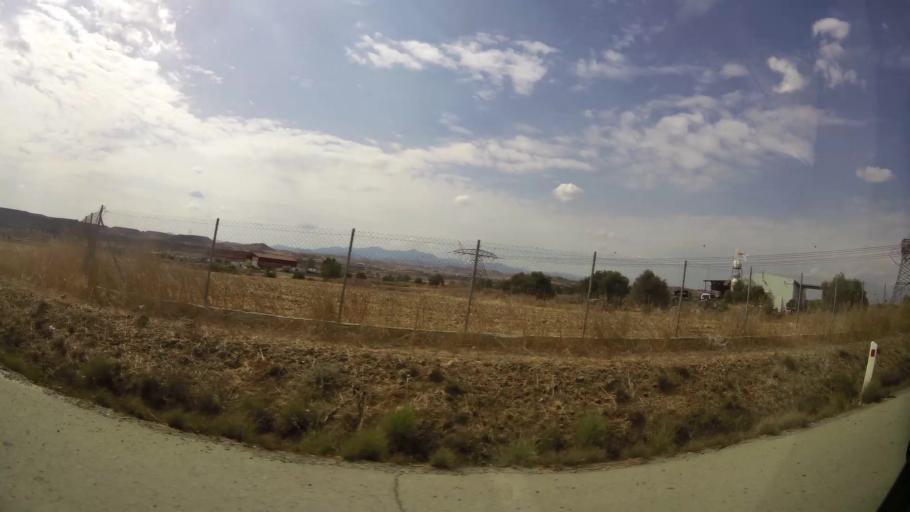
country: CY
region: Lefkosia
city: Tseri
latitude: 35.0635
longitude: 33.3439
